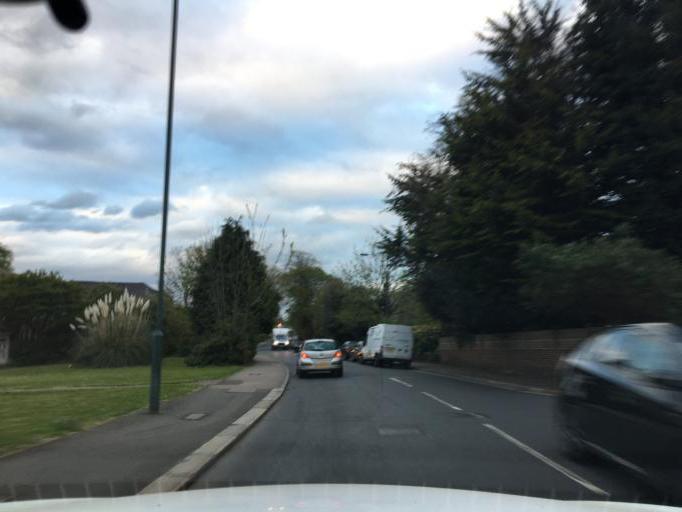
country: GB
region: England
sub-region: Greater London
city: Sidcup
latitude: 51.4287
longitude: 0.0895
